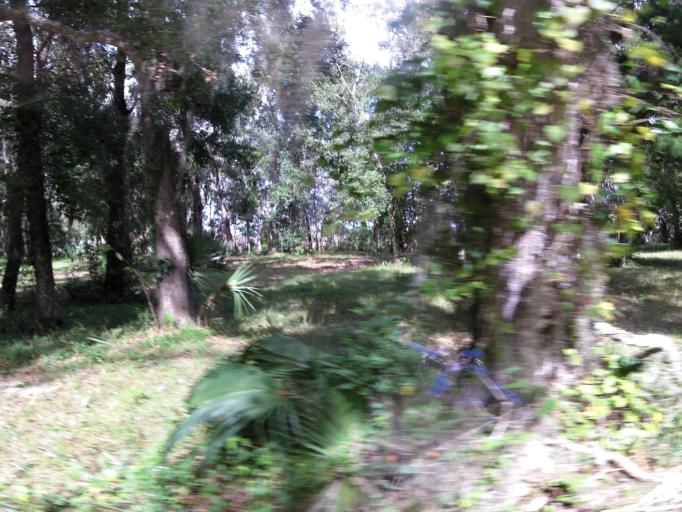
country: US
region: Florida
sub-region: Saint Johns County
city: Villano Beach
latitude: 29.9810
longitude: -81.3957
